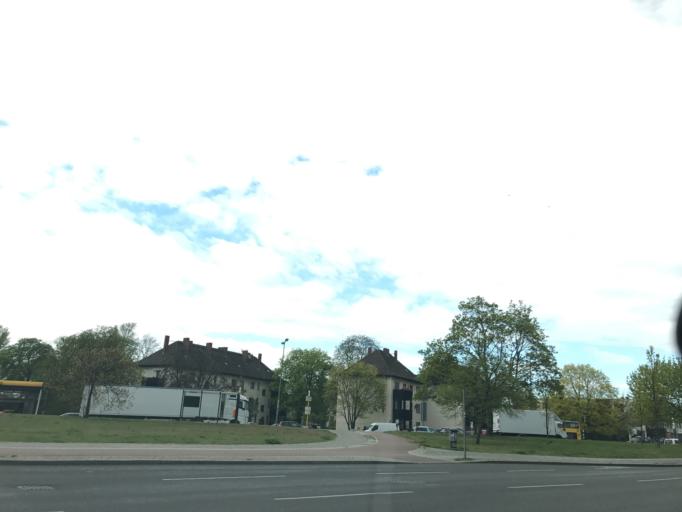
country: DE
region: Berlin
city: Reinickendorf
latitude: 52.5604
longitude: 13.3255
